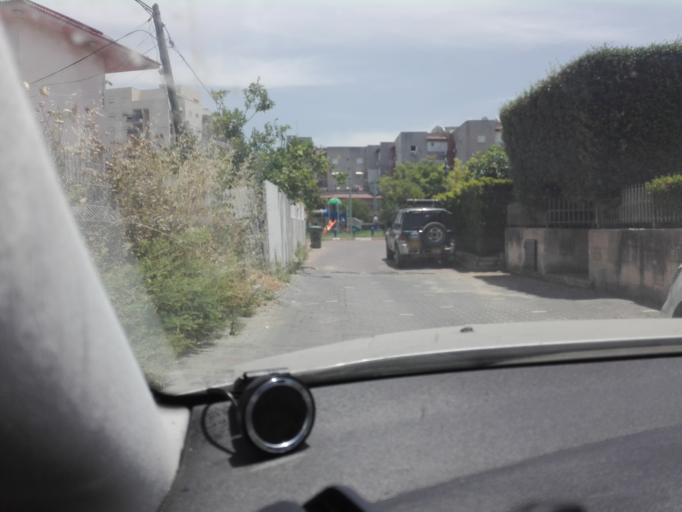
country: IL
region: Central District
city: Bene 'Ayish
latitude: 31.7353
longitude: 34.7445
